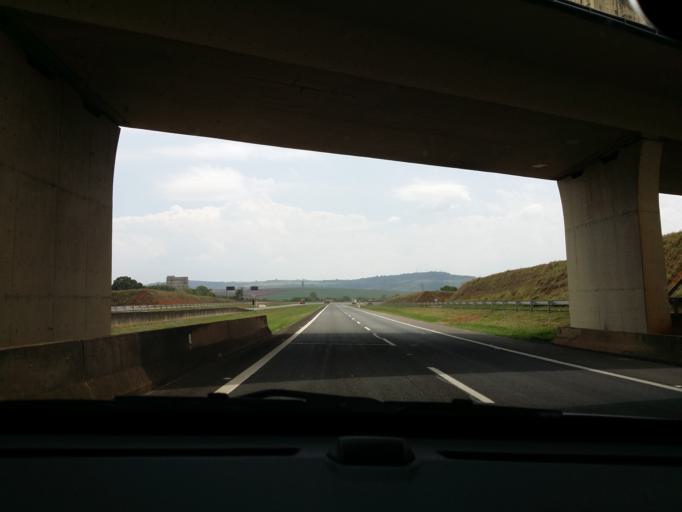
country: BR
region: Sao Paulo
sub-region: Limeira
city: Limeira
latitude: -22.5857
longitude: -47.4576
